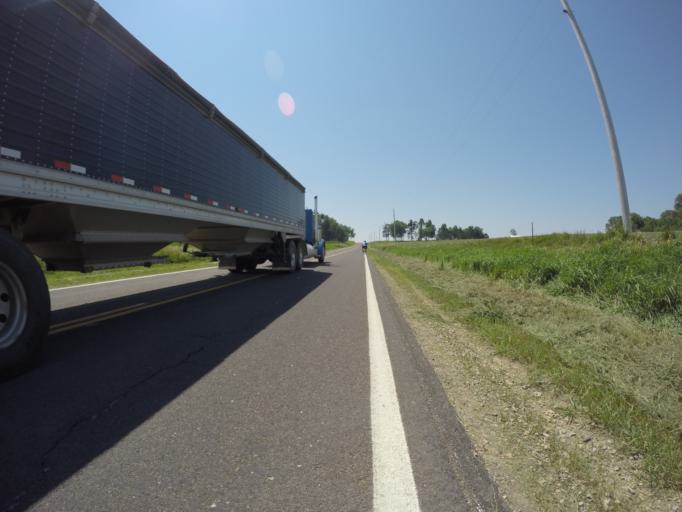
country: US
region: Kansas
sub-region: Doniphan County
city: Highland
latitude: 39.8355
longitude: -95.2653
